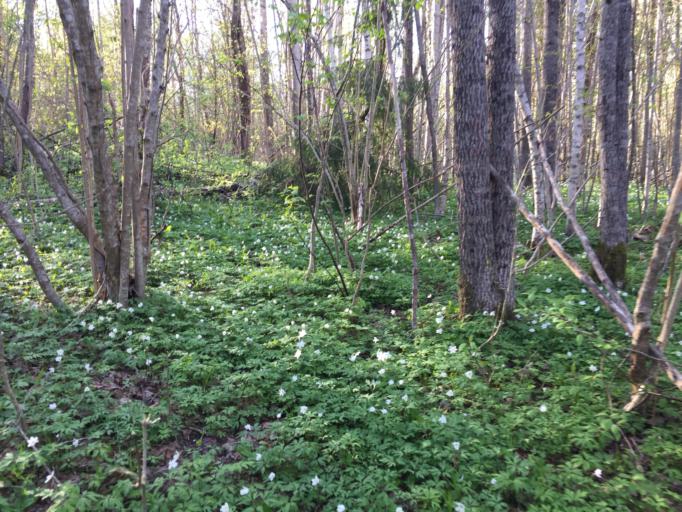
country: LV
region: Vecpiebalga
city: Vecpiebalga
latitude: 56.8670
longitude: 25.9482
